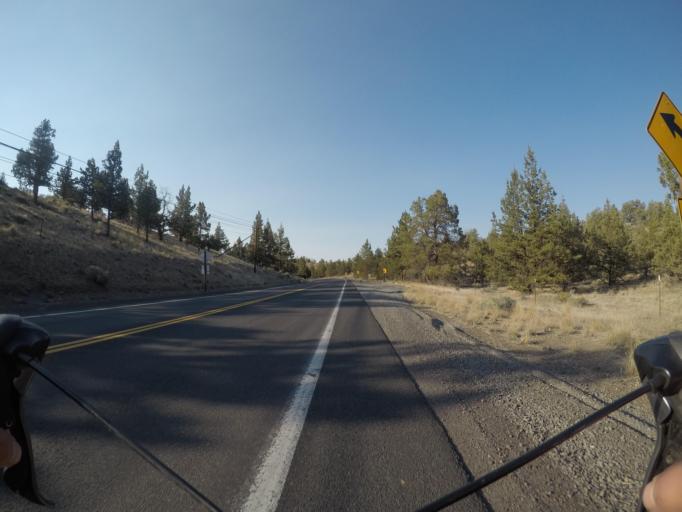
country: US
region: Oregon
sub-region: Deschutes County
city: Redmond
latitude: 44.2694
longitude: -121.2600
